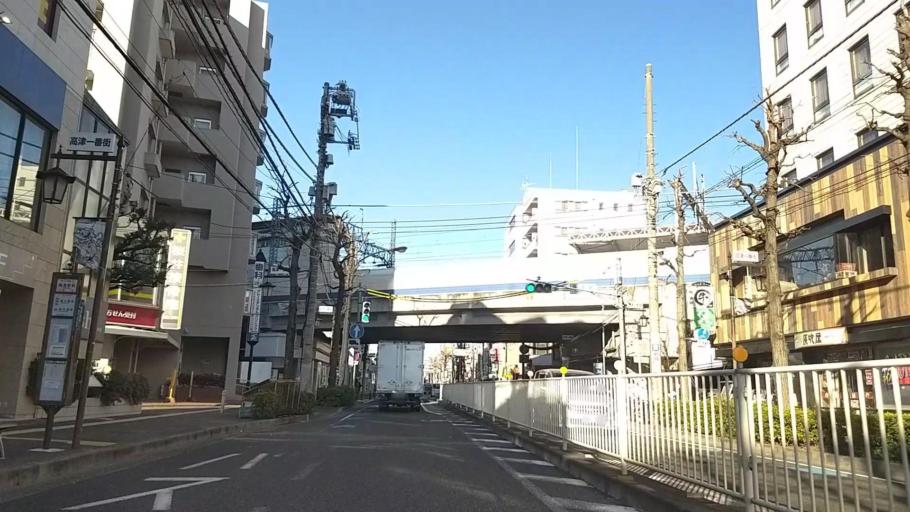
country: JP
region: Tokyo
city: Chofugaoka
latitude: 35.6027
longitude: 139.6170
